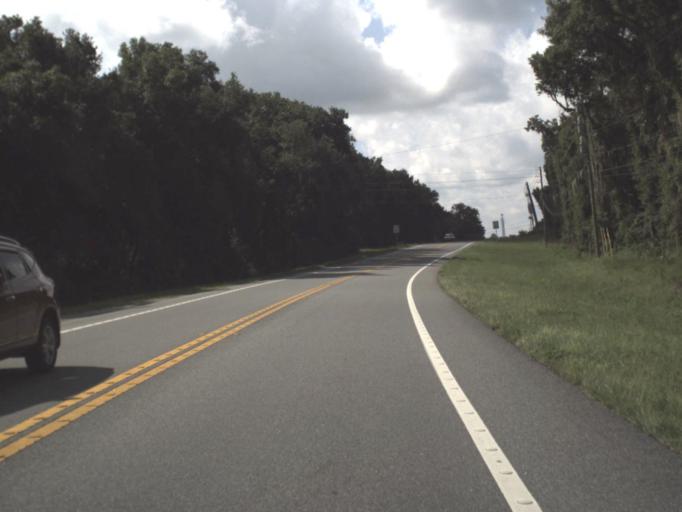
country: US
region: Florida
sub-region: Citrus County
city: Hernando
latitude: 28.9090
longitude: -82.3791
